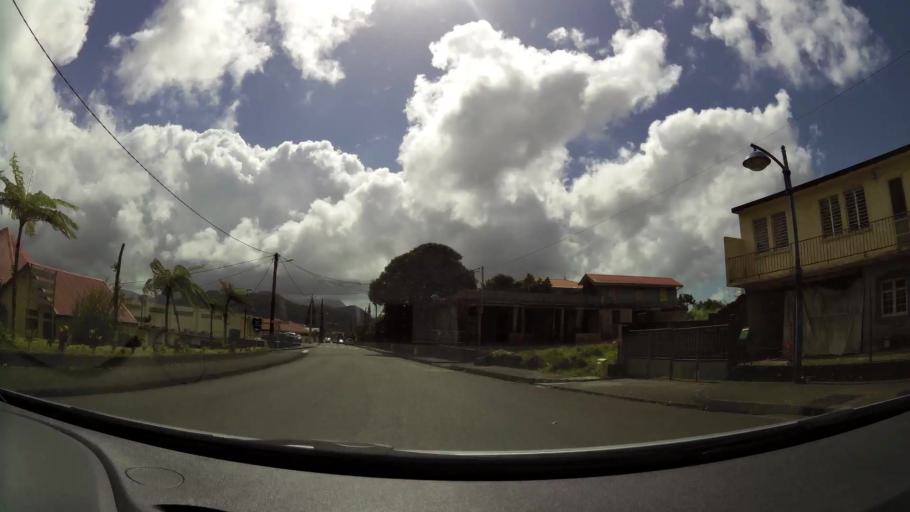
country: MQ
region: Martinique
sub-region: Martinique
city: Le Morne-Rouge
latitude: 14.7788
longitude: -61.1368
